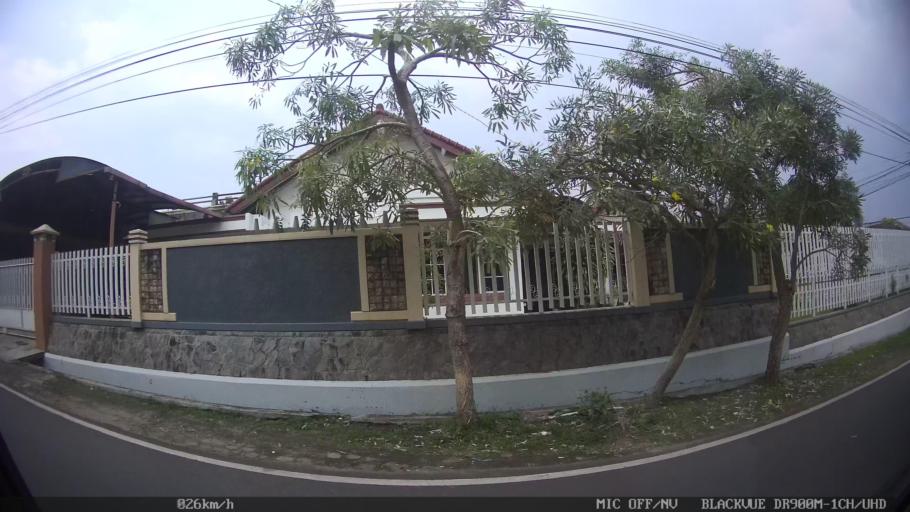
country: ID
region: Lampung
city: Bandarlampung
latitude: -5.4252
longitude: 105.2661
